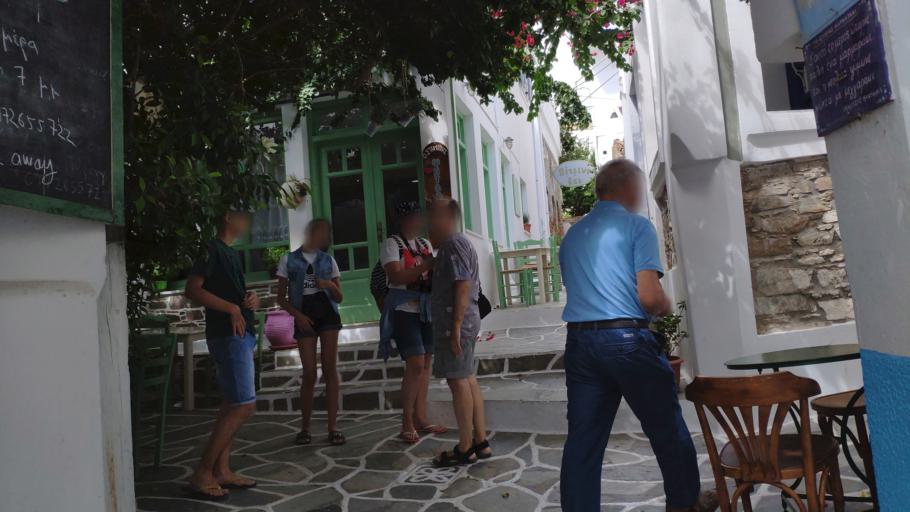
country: GR
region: South Aegean
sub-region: Nomos Kykladon
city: Kythnos
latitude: 37.3826
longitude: 24.4305
